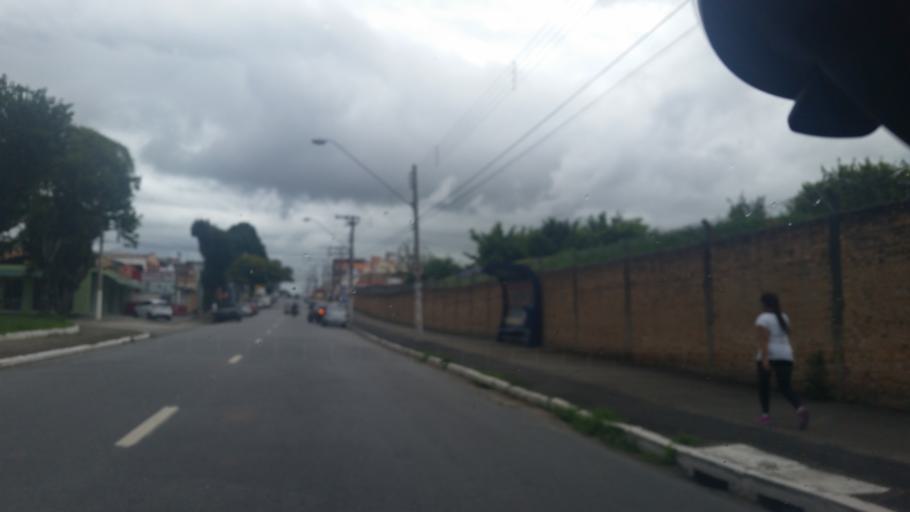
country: BR
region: Sao Paulo
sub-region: Taubate
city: Taubate
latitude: -23.0403
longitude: -45.5721
